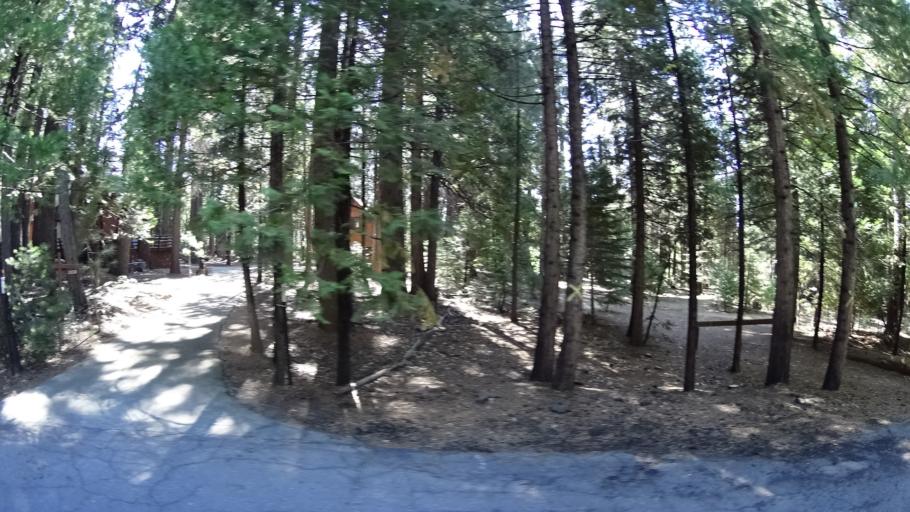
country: US
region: California
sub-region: Calaveras County
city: Arnold
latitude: 38.2901
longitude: -120.2689
